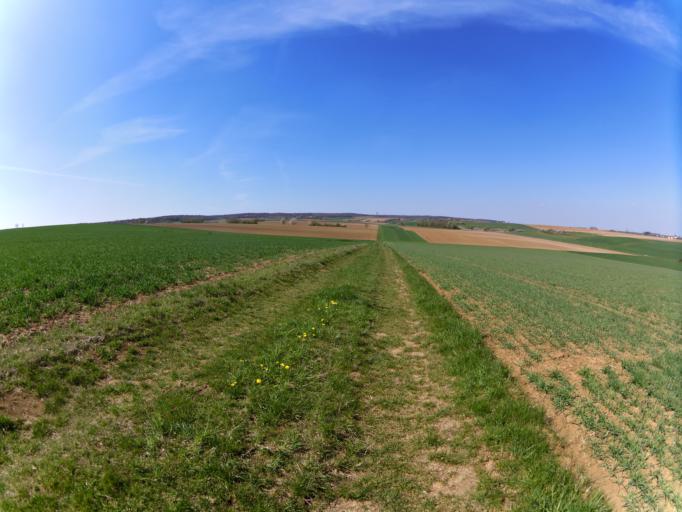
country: DE
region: Bavaria
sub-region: Regierungsbezirk Unterfranken
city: Kurnach
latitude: 49.8627
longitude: 10.0170
